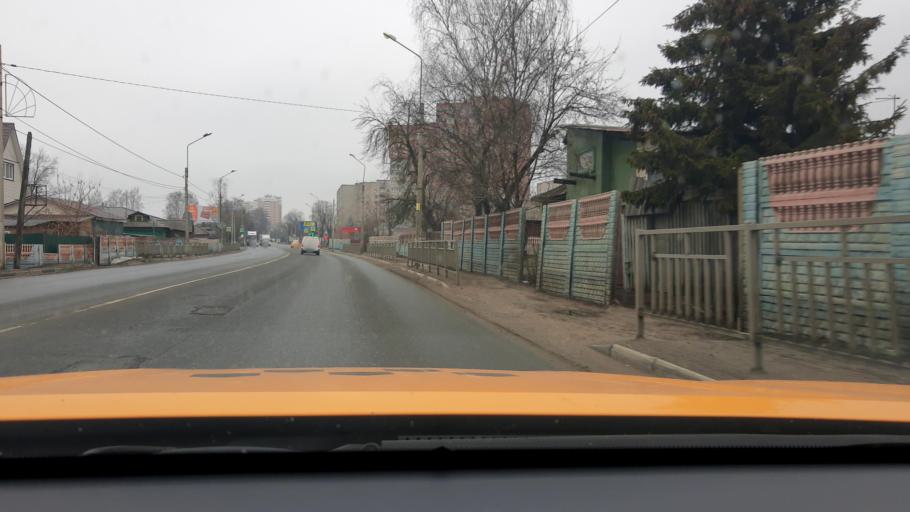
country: RU
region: Moskovskaya
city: Noginsk
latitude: 55.8720
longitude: 38.4356
